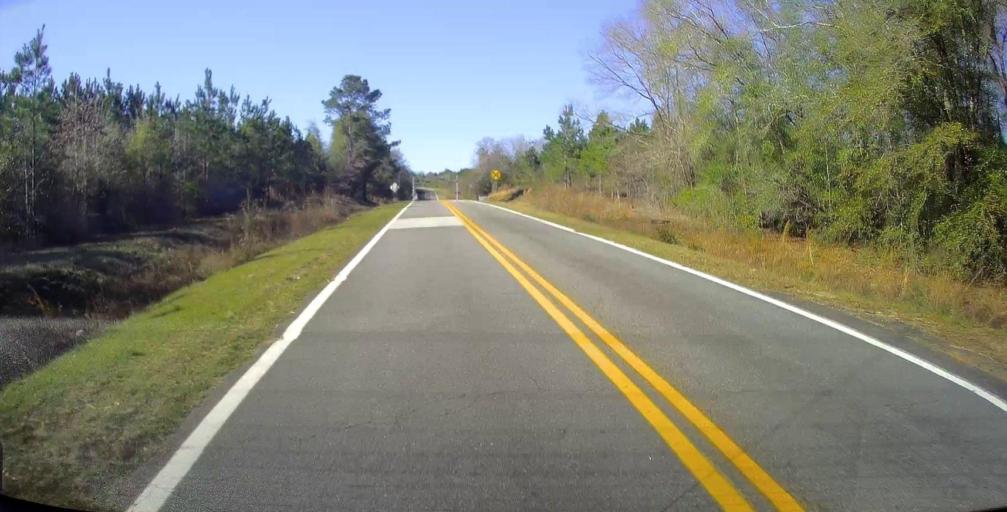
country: US
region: Georgia
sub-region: Taylor County
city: Reynolds
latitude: 32.5488
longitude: -83.9975
